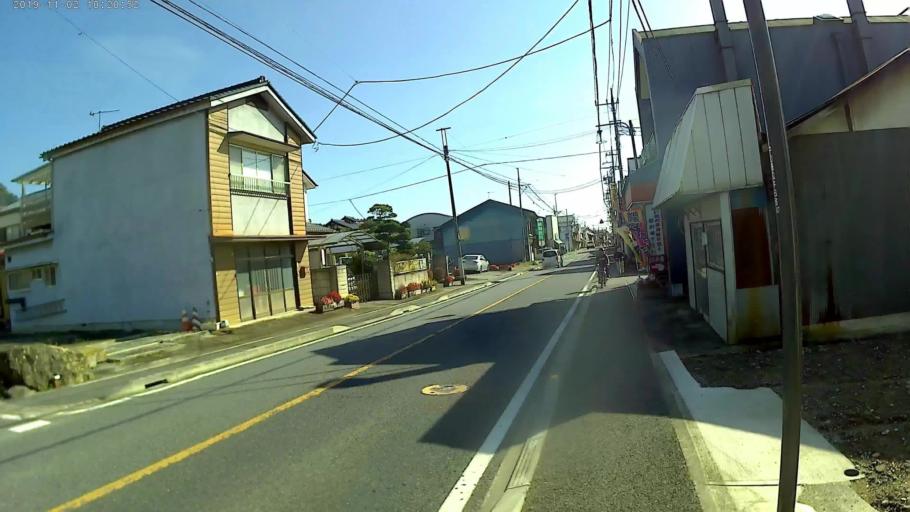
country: JP
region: Gunma
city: Annaka
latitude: 36.3143
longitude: 138.7989
